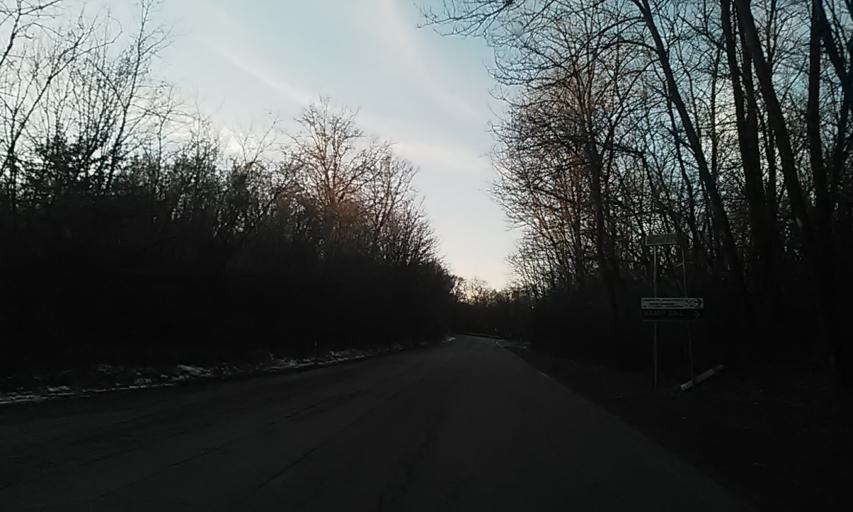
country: IT
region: Piedmont
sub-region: Provincia di Biella
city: Masserano
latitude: 45.5647
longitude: 8.2289
